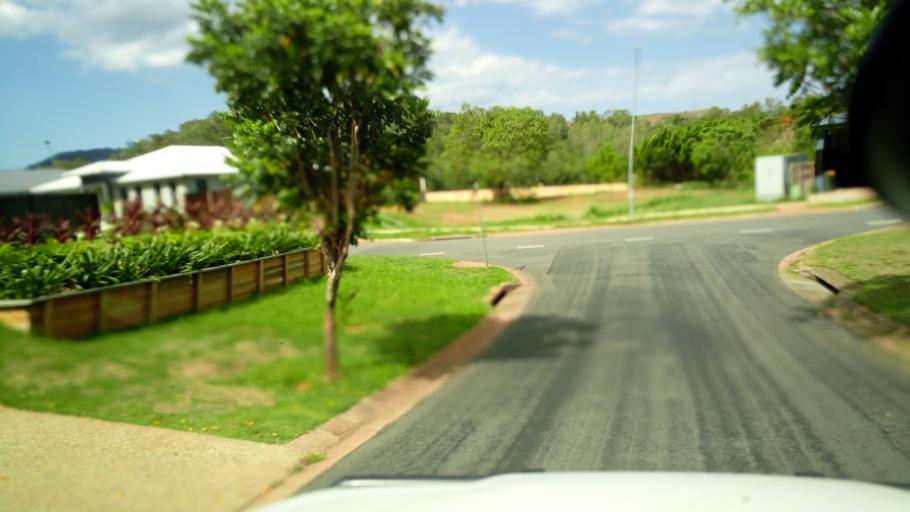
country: AU
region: Queensland
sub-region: Cairns
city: Woree
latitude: -16.9223
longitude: 145.7225
